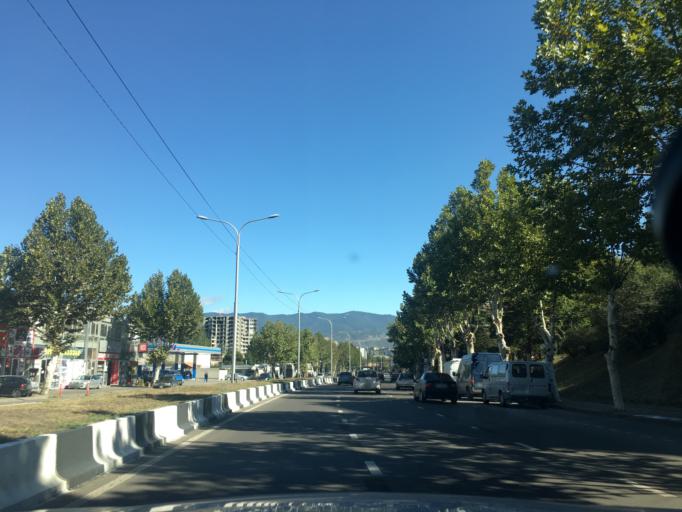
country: GE
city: Zahesi
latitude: 41.7796
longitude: 44.7964
